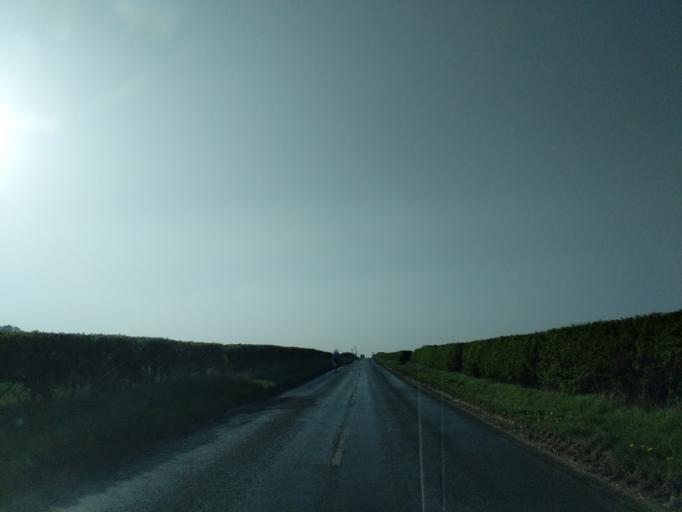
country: GB
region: Scotland
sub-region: Fife
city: Pathhead
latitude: 55.8808
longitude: -3.0166
